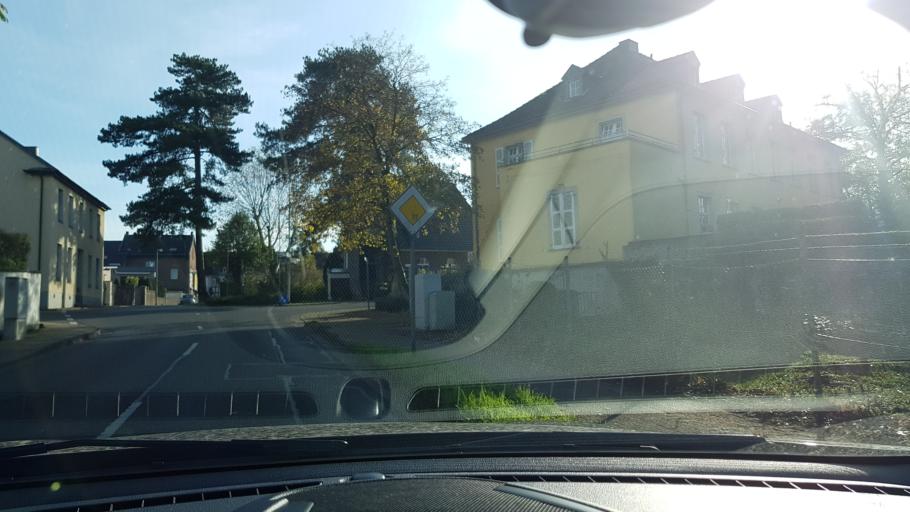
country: DE
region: North Rhine-Westphalia
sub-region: Regierungsbezirk Dusseldorf
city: Grevenbroich
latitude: 51.1050
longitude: 6.6165
